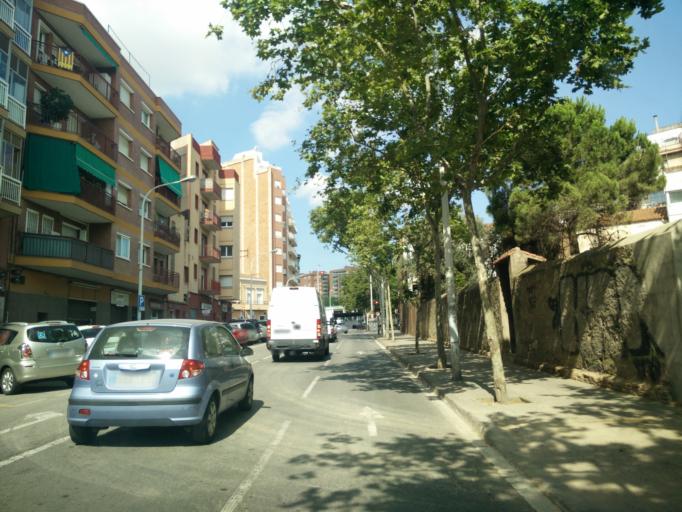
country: ES
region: Catalonia
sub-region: Provincia de Barcelona
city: Badalona
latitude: 41.4485
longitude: 2.2389
